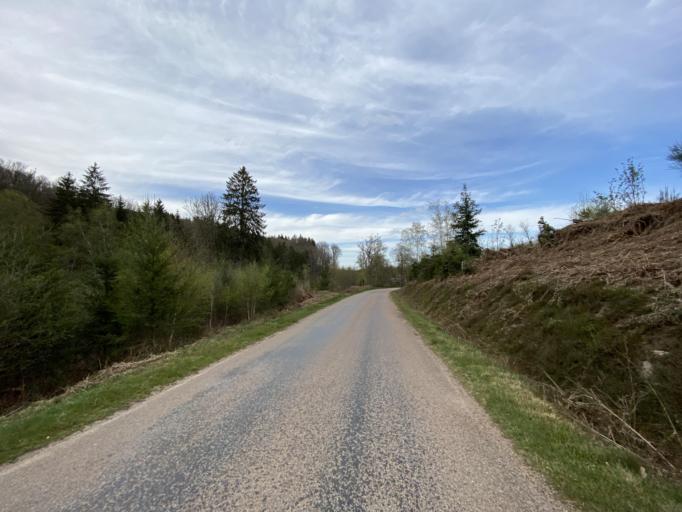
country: FR
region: Bourgogne
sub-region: Departement de la Cote-d'Or
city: Saulieu
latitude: 47.3155
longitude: 4.0938
